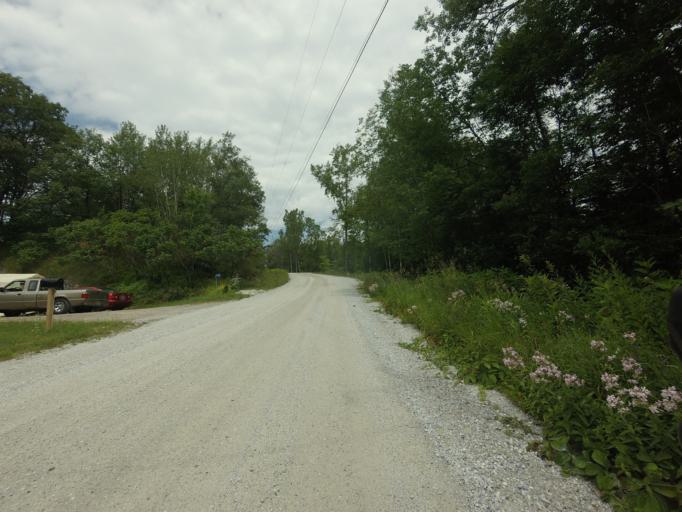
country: CA
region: Ontario
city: Perth
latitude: 44.7368
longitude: -76.6084
